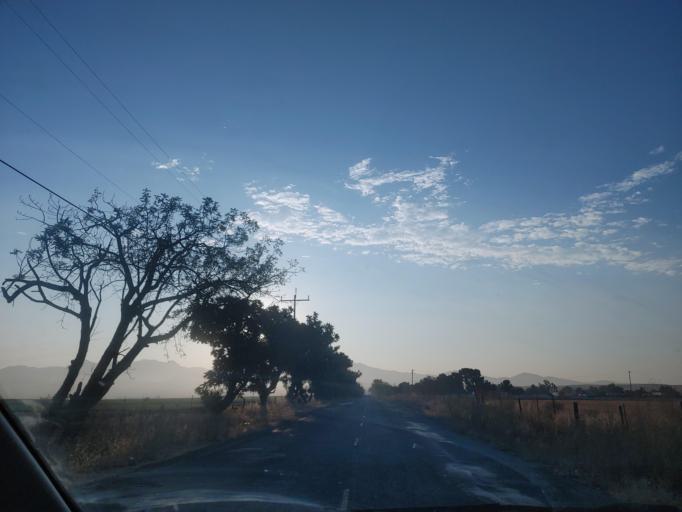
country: US
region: California
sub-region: San Benito County
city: Hollister
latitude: 36.8610
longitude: -121.3616
